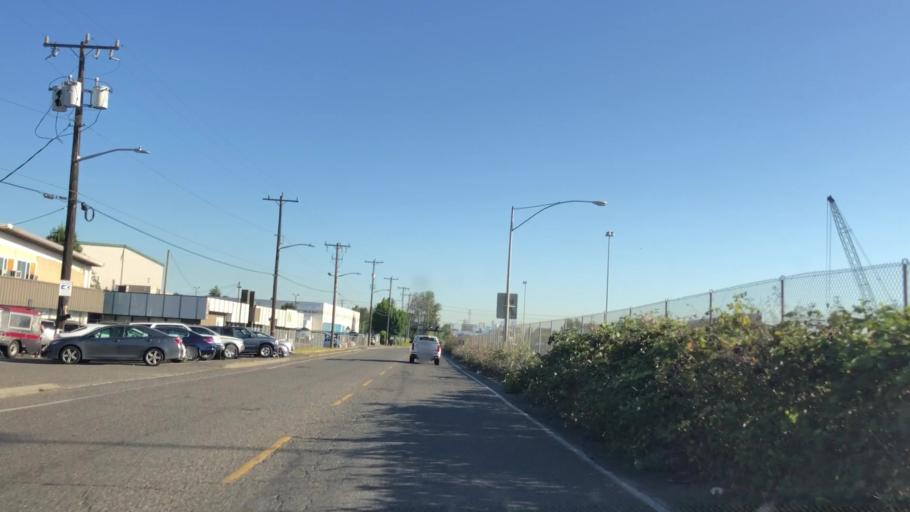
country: US
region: Washington
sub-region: King County
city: White Center
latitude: 47.5289
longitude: -122.3348
